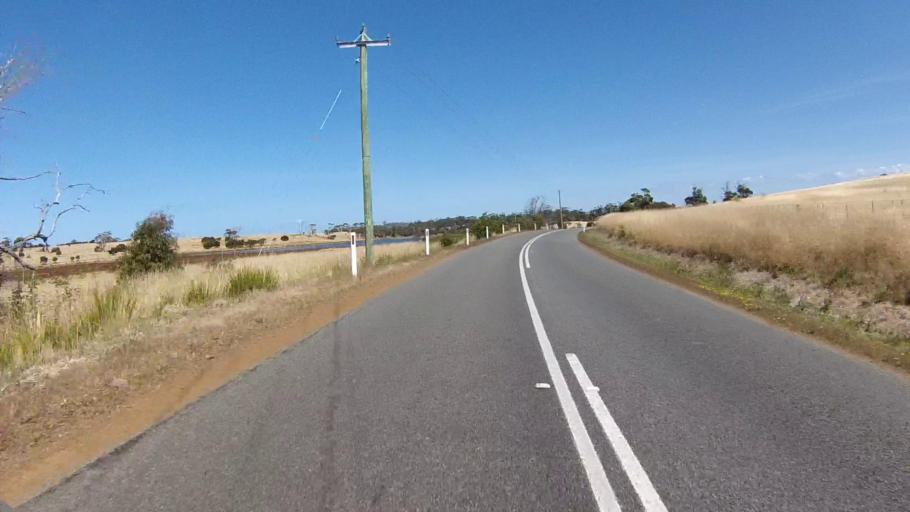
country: AU
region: Tasmania
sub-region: Sorell
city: Sorell
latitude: -42.2761
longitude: 148.0043
